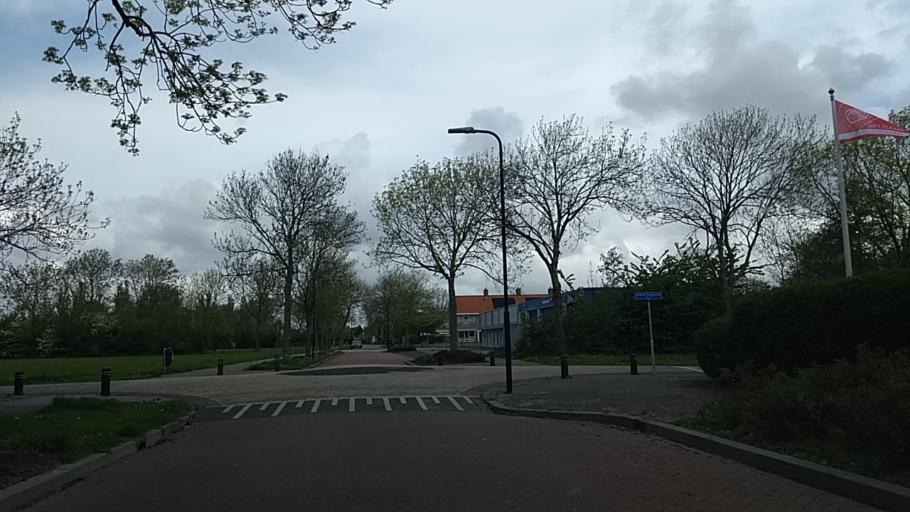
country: NL
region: Friesland
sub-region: Gemeente Harlingen
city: Harlingen
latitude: 53.1673
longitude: 5.4355
